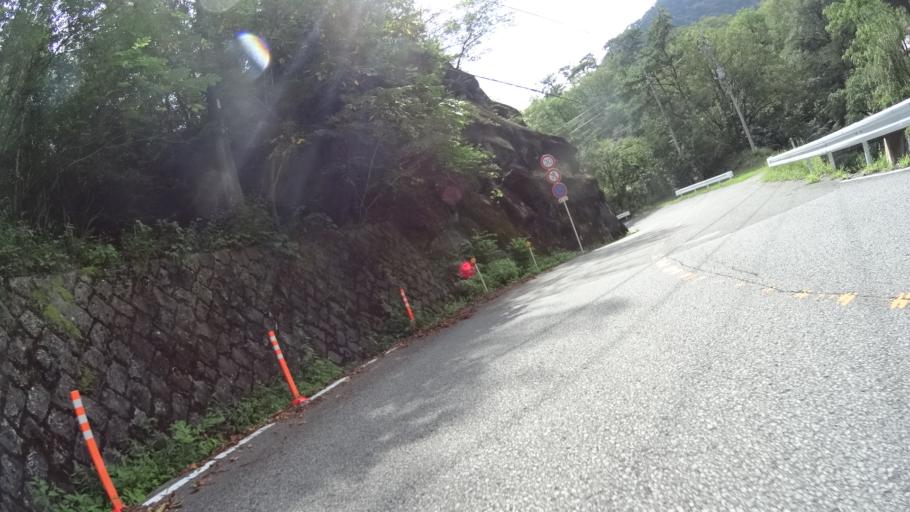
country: JP
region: Yamanashi
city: Kofu-shi
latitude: 35.7421
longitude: 138.5678
